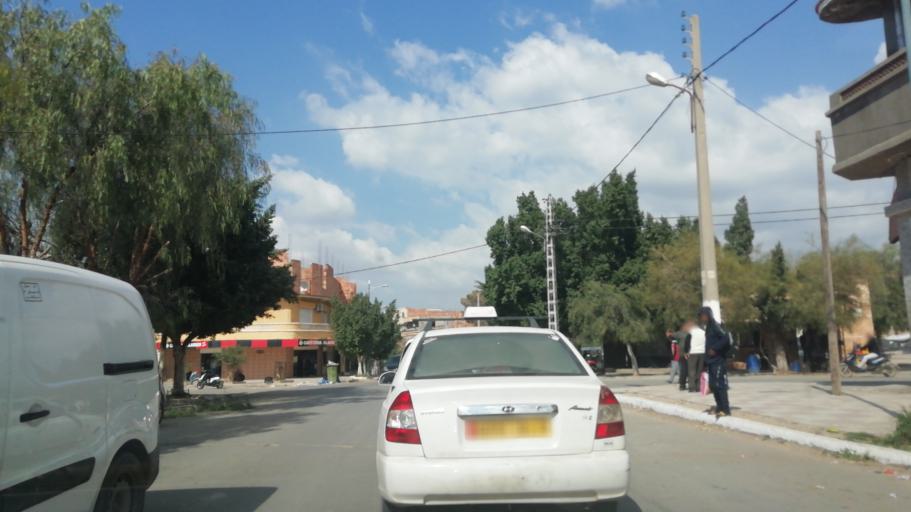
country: DZ
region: Mascara
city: Mascara
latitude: 35.5811
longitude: 0.0702
